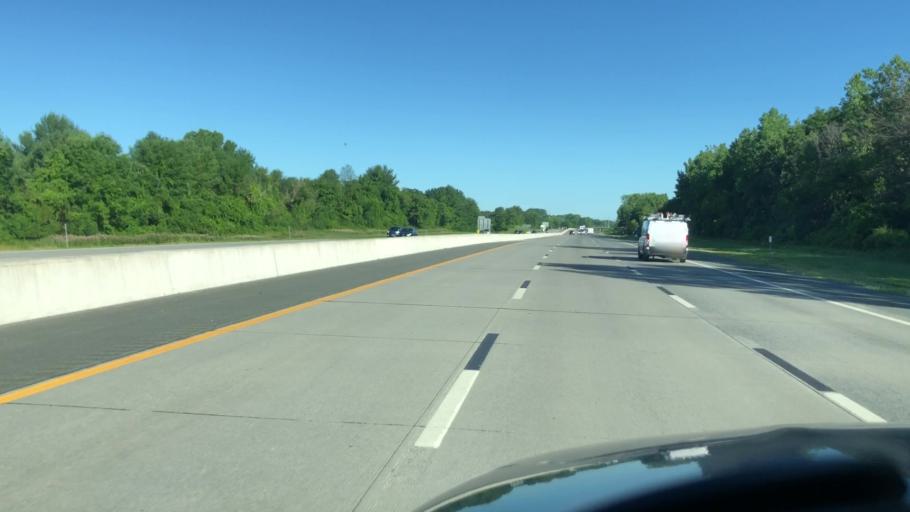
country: US
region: New York
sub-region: Albany County
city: Delmar
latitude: 42.6456
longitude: -73.8070
